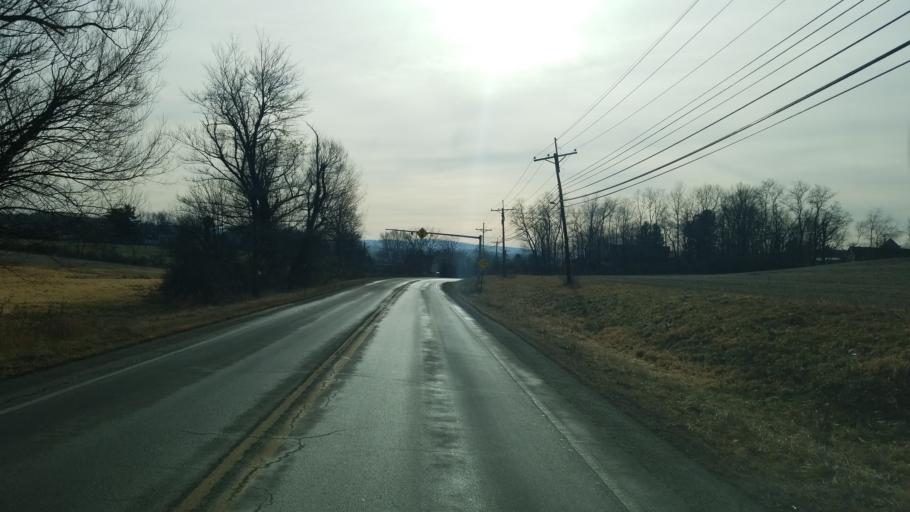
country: US
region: Pennsylvania
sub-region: Indiana County
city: Indiana
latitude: 40.6052
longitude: -79.1479
